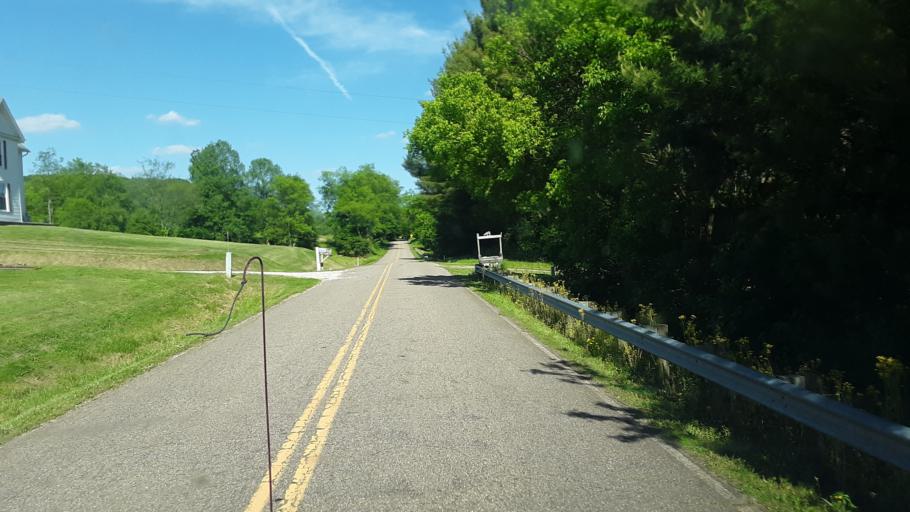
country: US
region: Ohio
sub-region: Tuscarawas County
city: Newcomerstown
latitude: 40.1815
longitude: -81.6010
